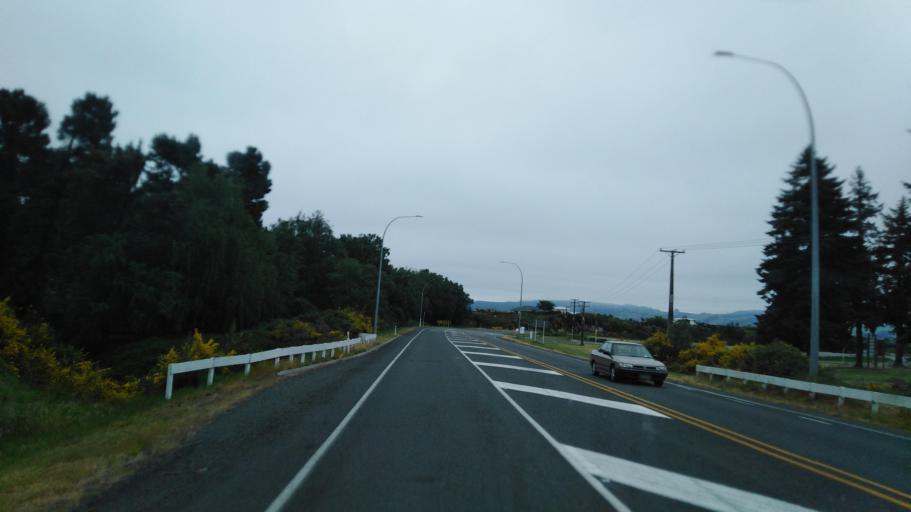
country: NZ
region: Waikato
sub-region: Taupo District
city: Taupo
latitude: -38.7056
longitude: 176.1060
